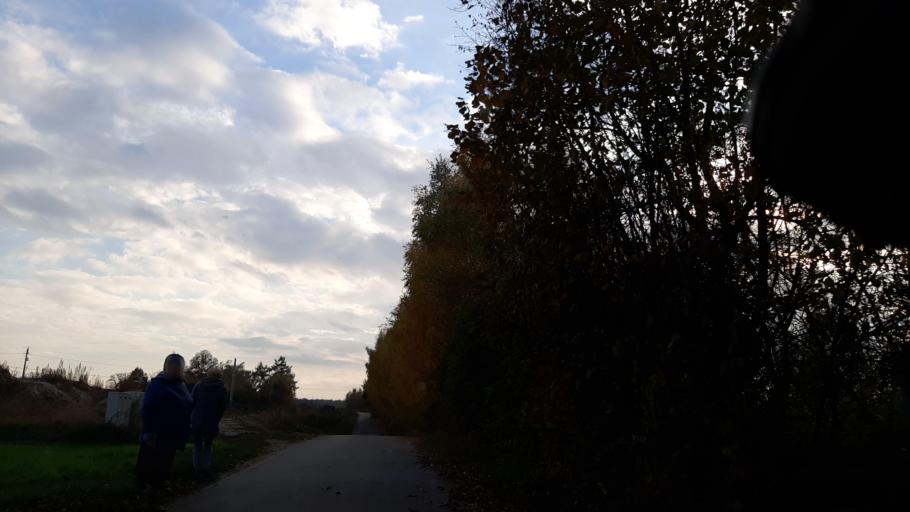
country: PL
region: Lublin Voivodeship
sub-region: Powiat lubelski
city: Garbow
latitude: 51.3451
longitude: 22.3201
